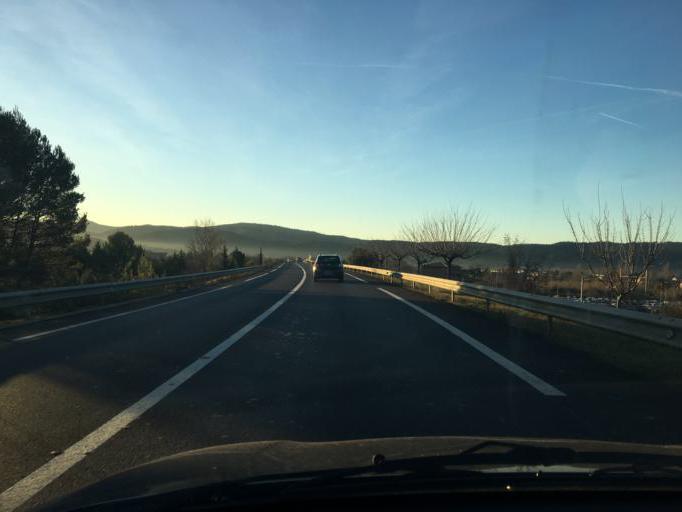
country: FR
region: Provence-Alpes-Cote d'Azur
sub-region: Departement du Var
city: Les Arcs
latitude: 43.4593
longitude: 6.4879
